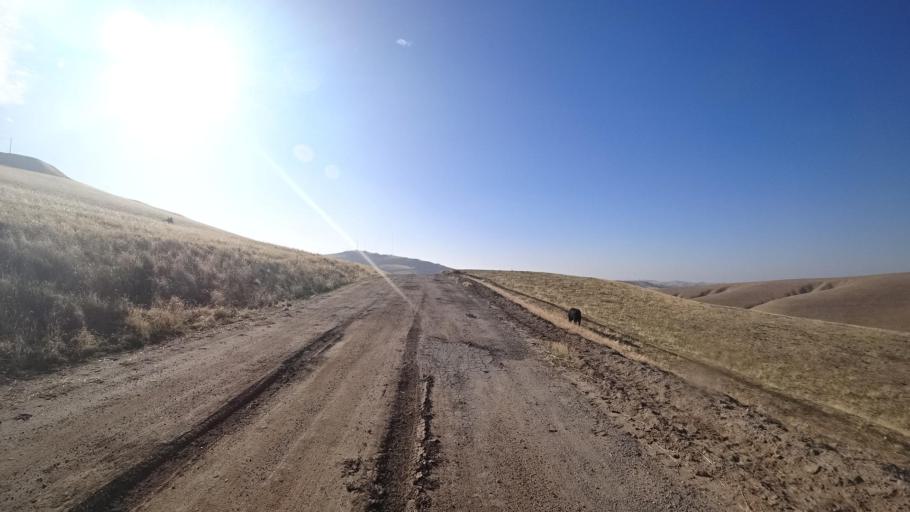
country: US
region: California
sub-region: Kern County
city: Oildale
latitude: 35.4911
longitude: -118.8781
